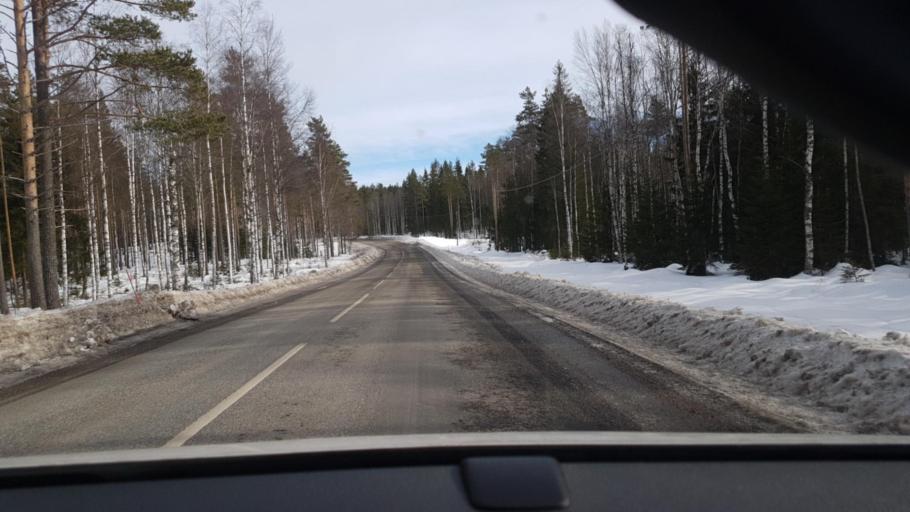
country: SE
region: Vaermland
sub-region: Arjangs Kommun
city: Arjaeng
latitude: 59.5644
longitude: 12.1980
